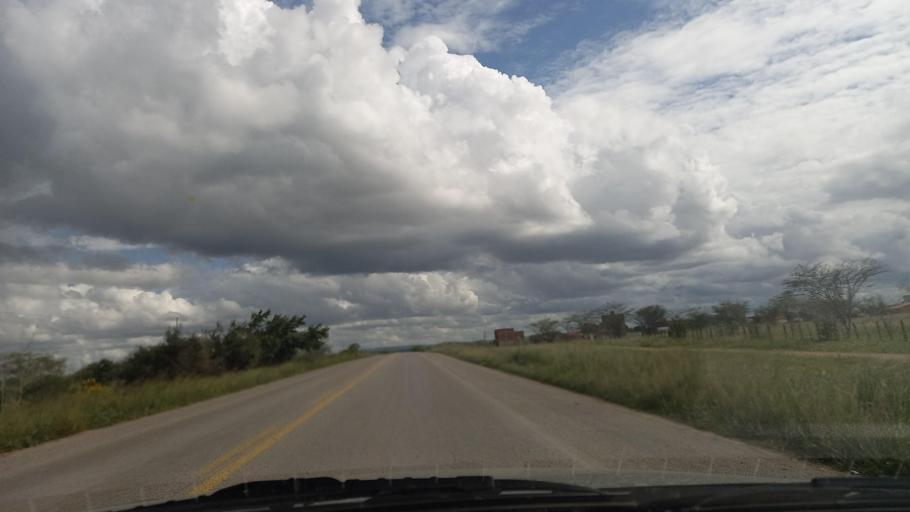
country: BR
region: Pernambuco
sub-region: Cachoeirinha
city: Cachoeirinha
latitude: -8.4980
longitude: -36.2423
